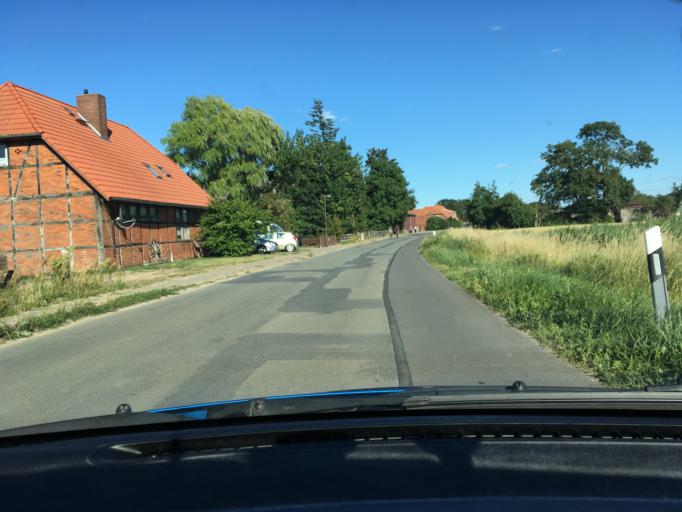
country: DE
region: Mecklenburg-Vorpommern
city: Boizenburg
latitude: 53.3477
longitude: 10.7188
